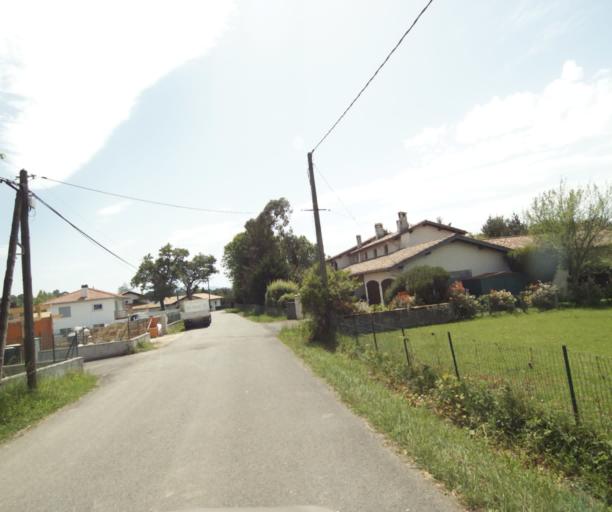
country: FR
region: Aquitaine
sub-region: Departement des Pyrenees-Atlantiques
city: Mouguerre
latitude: 43.4565
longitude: -1.4342
